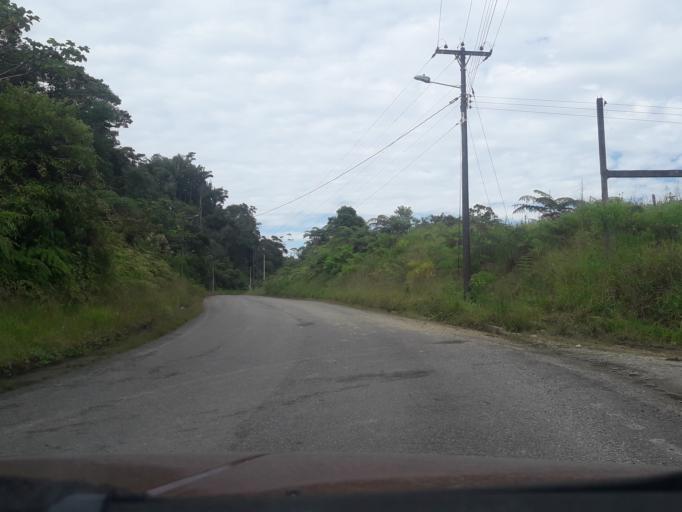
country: EC
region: Napo
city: Tena
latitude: -1.0259
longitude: -77.8866
